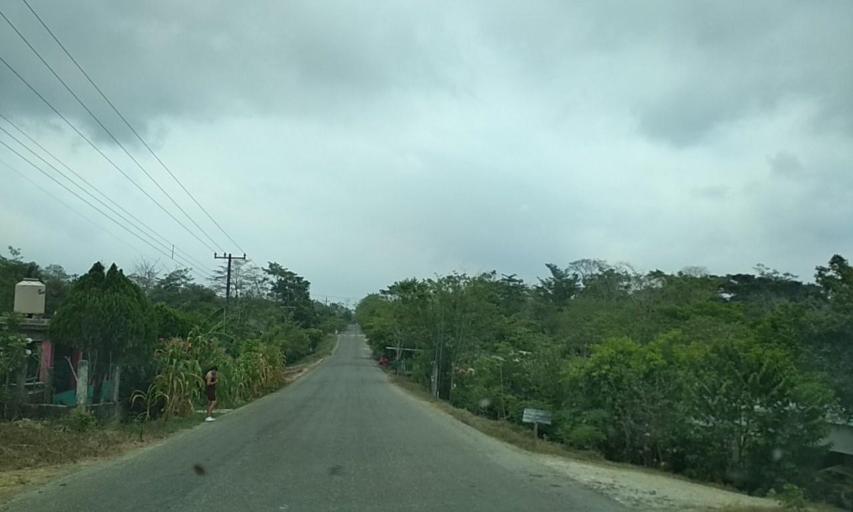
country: MX
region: Tabasco
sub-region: Huimanguillo
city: Francisco Rueda
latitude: 17.5695
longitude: -94.1106
